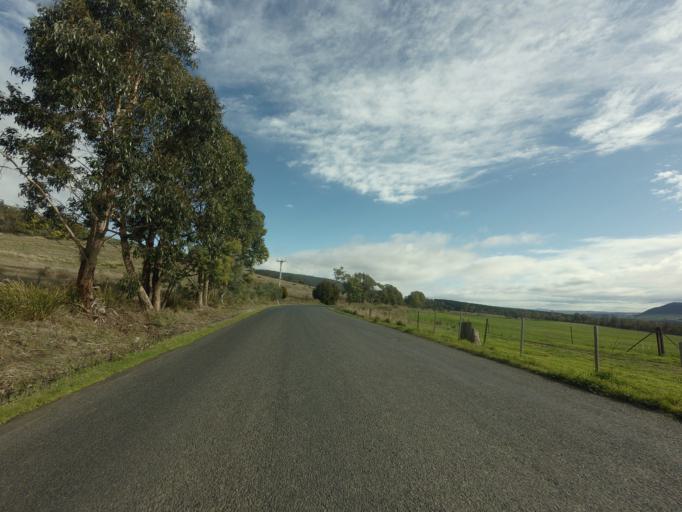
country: AU
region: Tasmania
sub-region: Derwent Valley
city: New Norfolk
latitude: -42.7794
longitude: 146.9869
